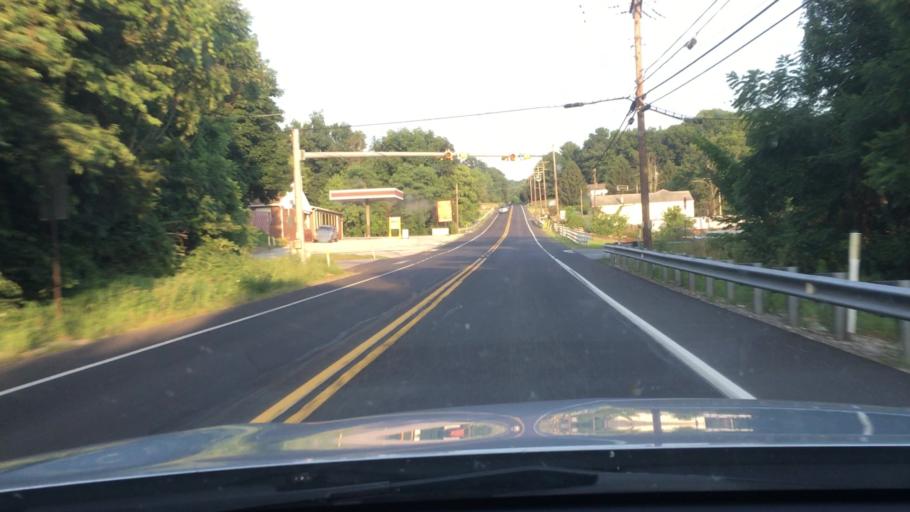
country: US
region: Pennsylvania
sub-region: York County
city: Dover
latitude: 40.0385
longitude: -76.8892
